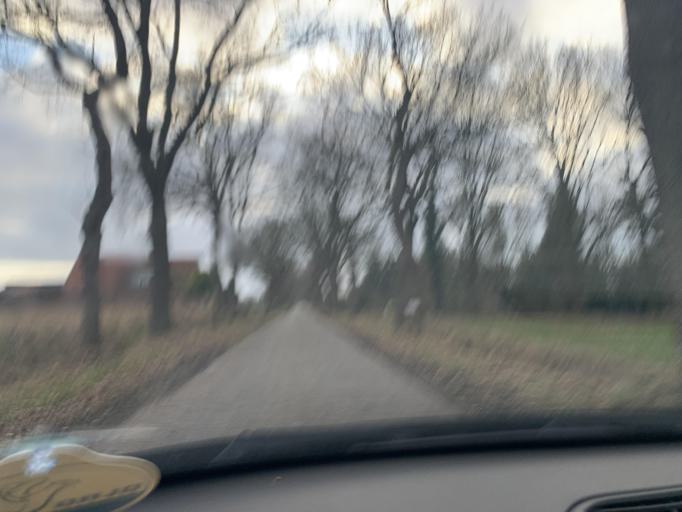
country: DE
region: Lower Saxony
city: Westerstede
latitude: 53.3005
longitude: 7.9341
